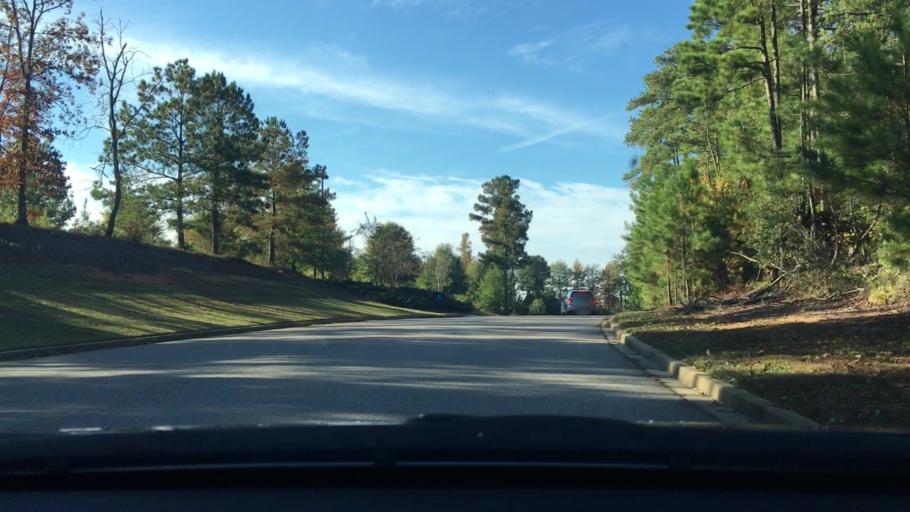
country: US
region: South Carolina
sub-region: Lexington County
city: Irmo
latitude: 34.0866
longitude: -81.1534
